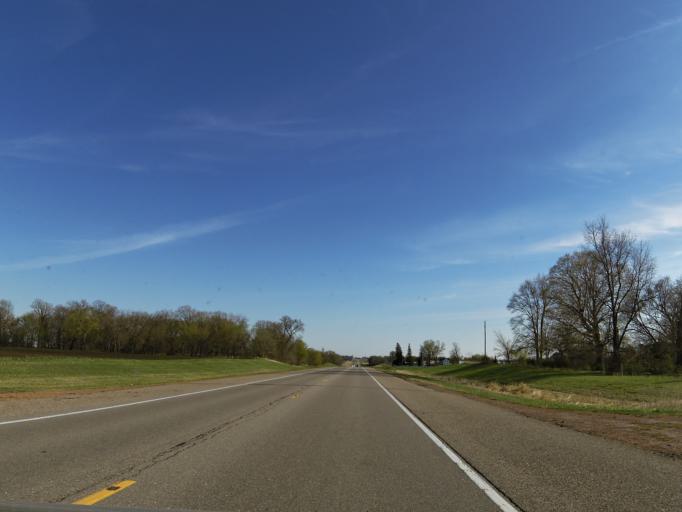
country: US
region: Minnesota
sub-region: Le Sueur County
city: New Prague
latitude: 44.6286
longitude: -93.5018
